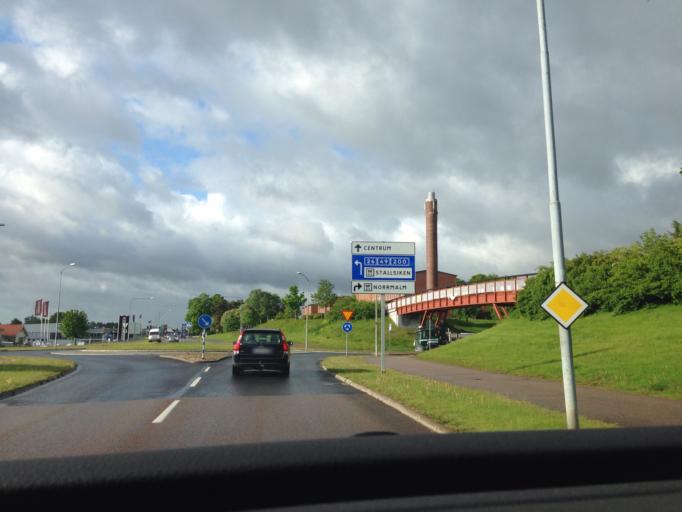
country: SE
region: Vaestra Goetaland
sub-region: Skovde Kommun
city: Skoevde
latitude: 58.4075
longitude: 13.8659
